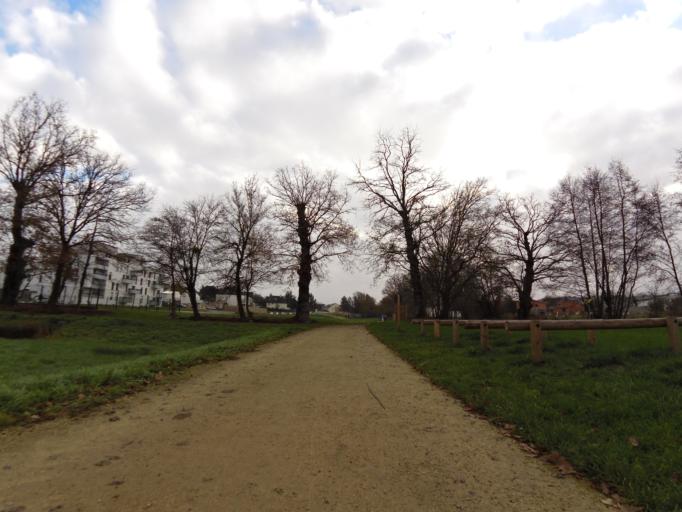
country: FR
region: Brittany
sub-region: Departement d'Ille-et-Vilaine
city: Orgeres
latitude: 47.9956
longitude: -1.6739
